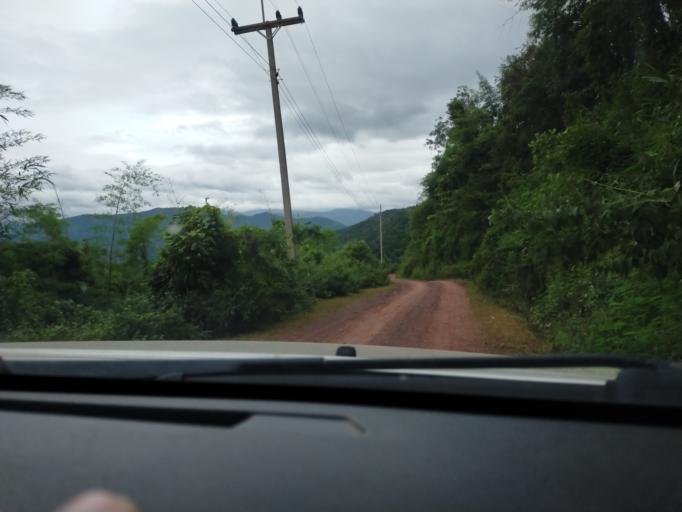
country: TH
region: Nan
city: Chaloem Phra Kiat
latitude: 19.7768
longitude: 101.3566
